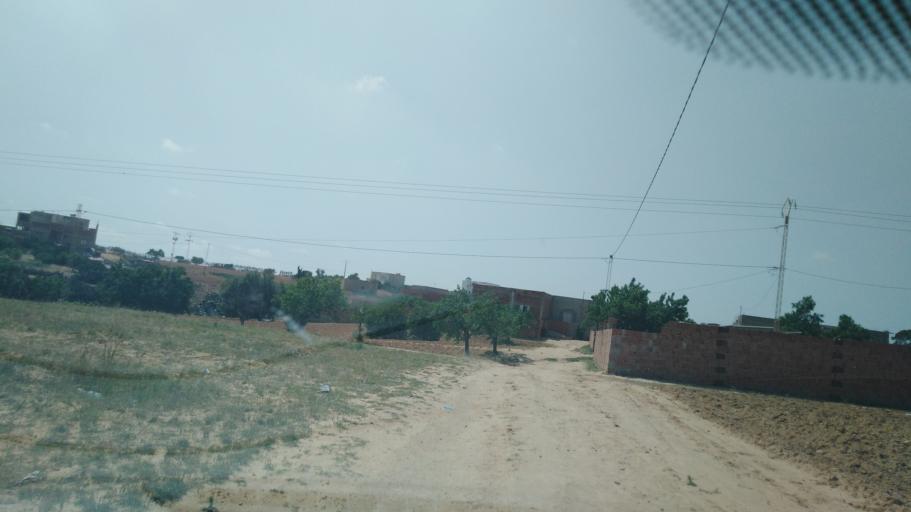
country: TN
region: Safaqis
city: Sfax
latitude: 34.7289
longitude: 10.5744
